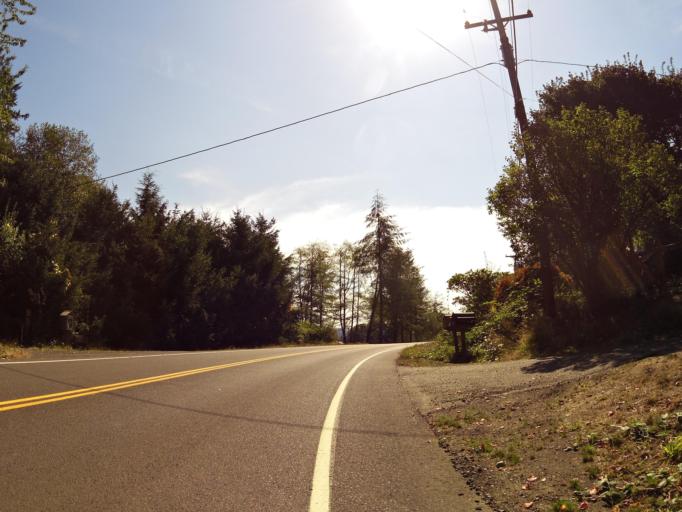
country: US
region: Washington
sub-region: Wahkiakum County
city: Cathlamet
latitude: 46.1802
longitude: -123.5831
